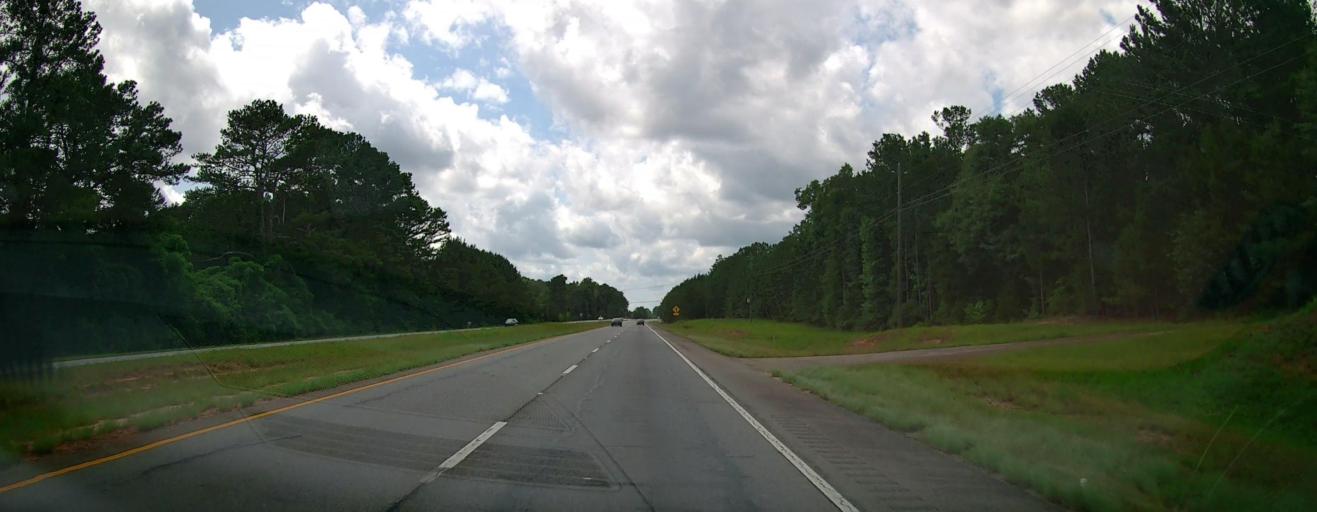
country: US
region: Georgia
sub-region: Heard County
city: Franklin
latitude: 33.2528
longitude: -85.0462
